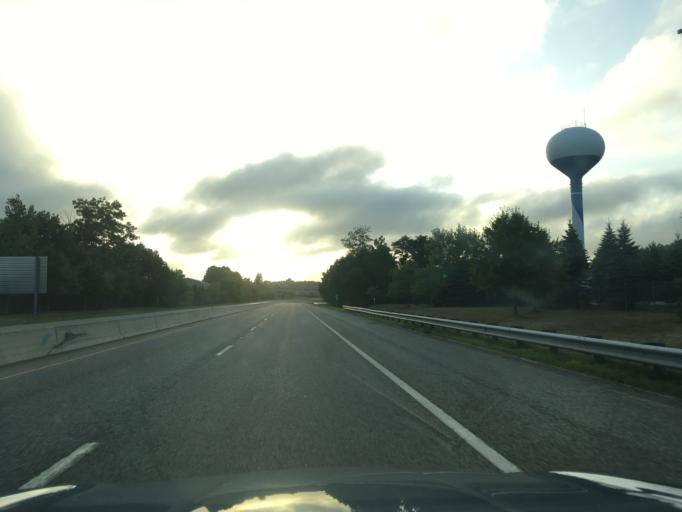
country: US
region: Rhode Island
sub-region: Kent County
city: East Greenwich
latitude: 41.6071
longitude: -71.4674
